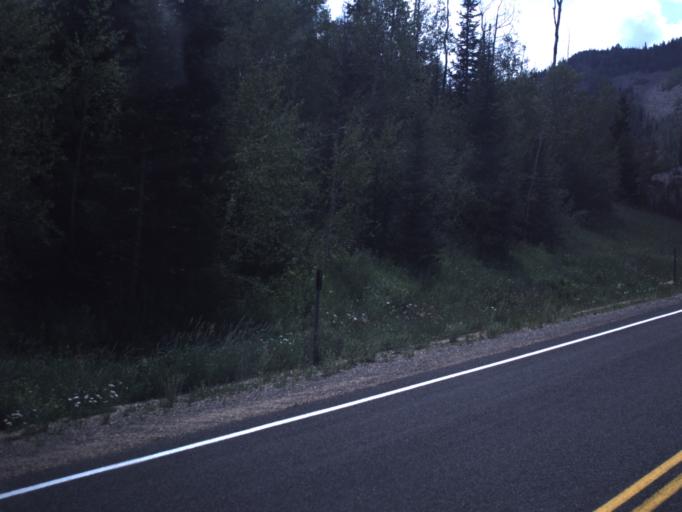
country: US
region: Utah
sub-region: Summit County
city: Francis
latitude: 40.5371
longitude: -111.0992
